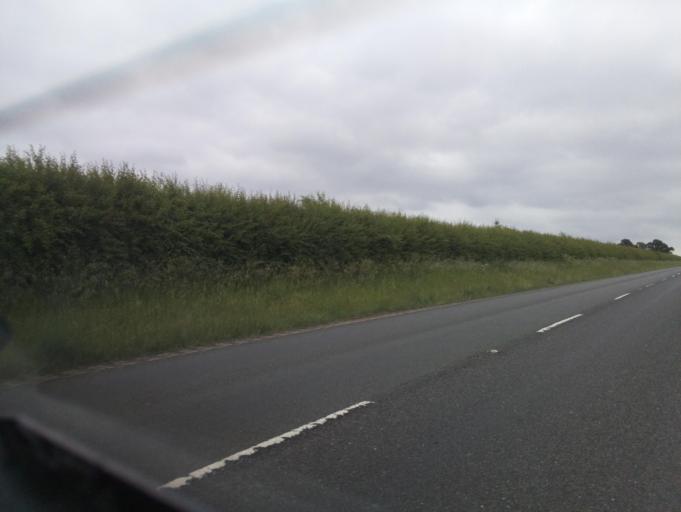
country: GB
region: England
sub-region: District of Rutland
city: Empingham
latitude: 52.6516
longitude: -0.6085
